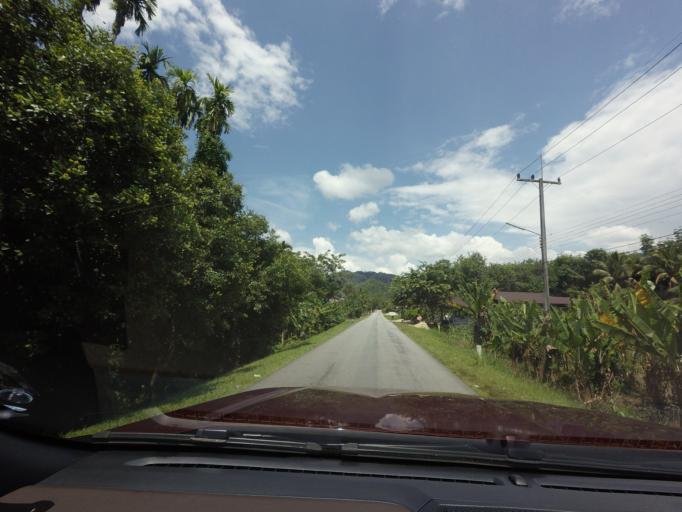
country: TH
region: Narathiwat
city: Chanae
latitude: 6.0907
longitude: 101.6916
